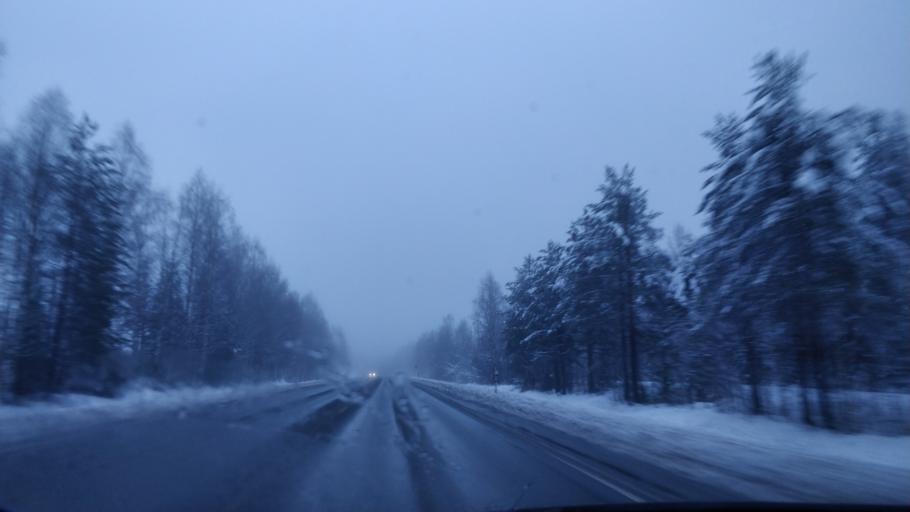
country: FI
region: Lapland
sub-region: Kemi-Tornio
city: Tervola
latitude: 66.1525
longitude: 25.0106
